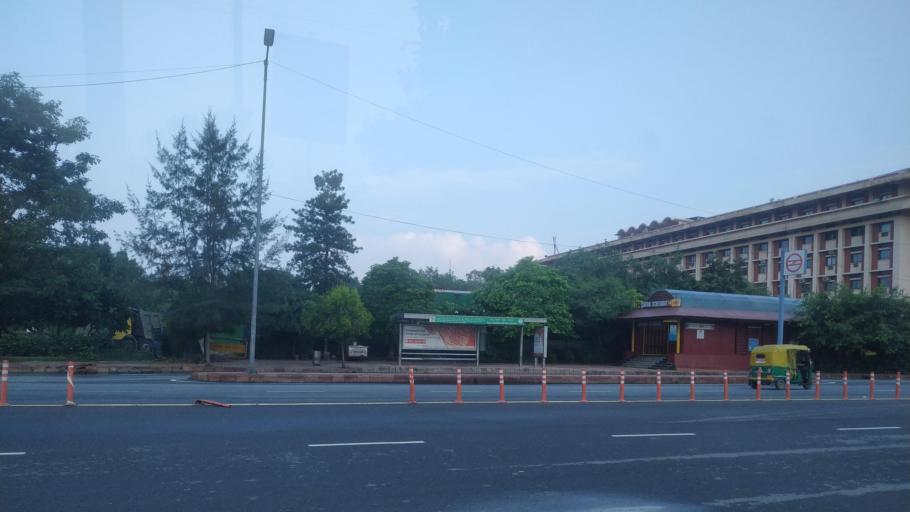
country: IN
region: NCT
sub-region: New Delhi
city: New Delhi
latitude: 28.6148
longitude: 77.2123
